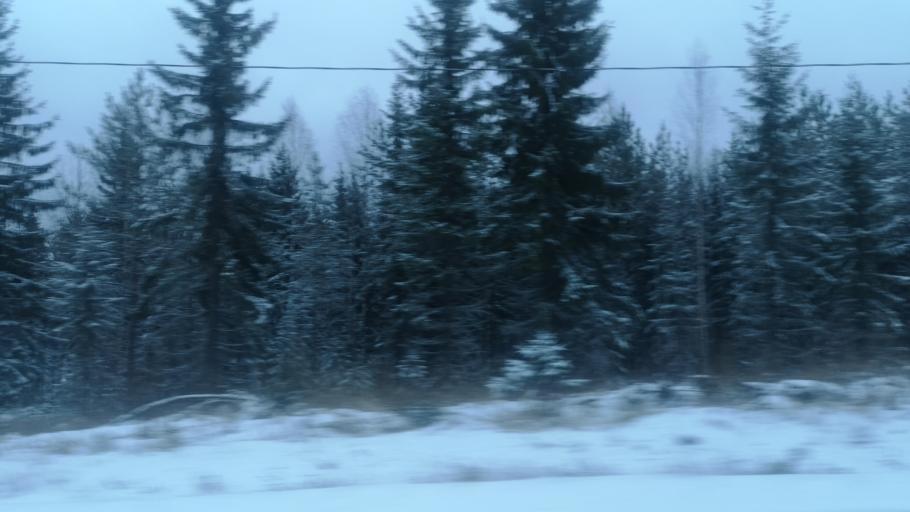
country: FI
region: Southern Savonia
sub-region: Savonlinna
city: Enonkoski
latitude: 62.0520
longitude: 28.7040
